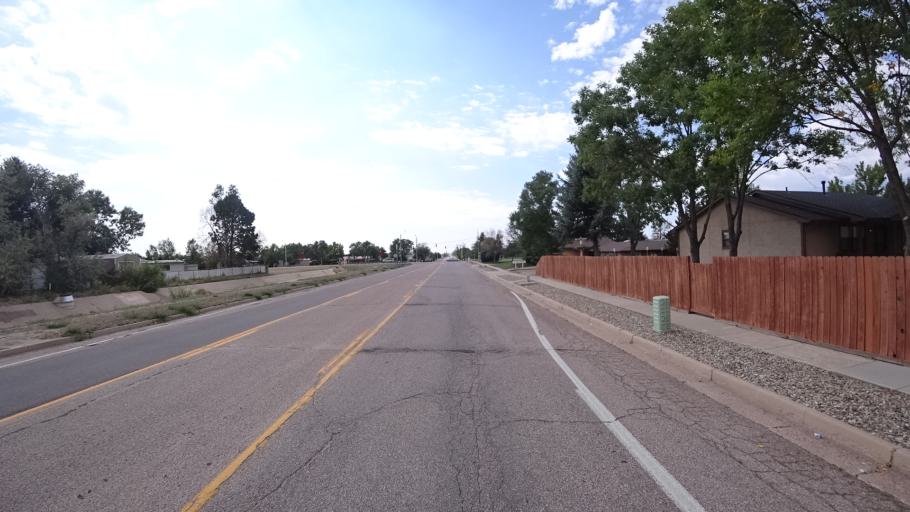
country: US
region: Colorado
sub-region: El Paso County
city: Cimarron Hills
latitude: 38.8483
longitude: -104.7387
